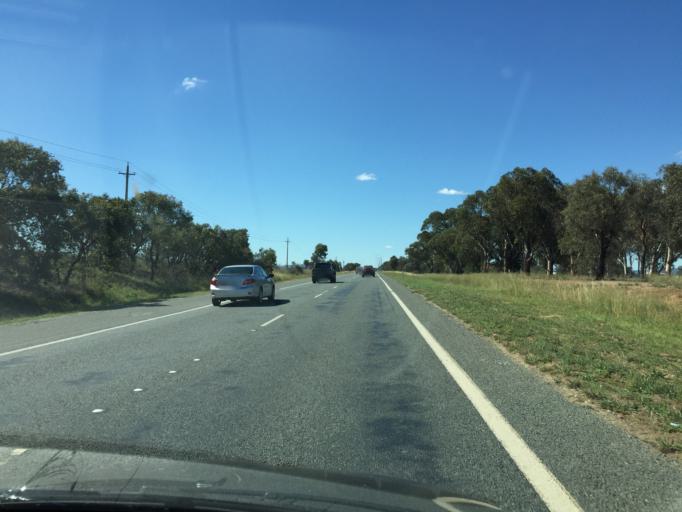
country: AU
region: Australian Capital Territory
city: Macarthur
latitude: -35.3779
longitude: 149.1694
